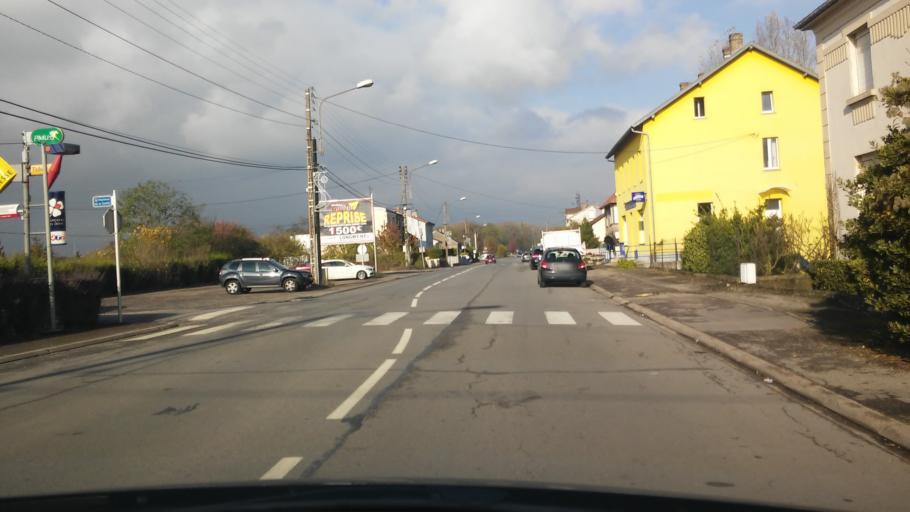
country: FR
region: Lorraine
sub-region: Departement de la Moselle
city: Richemont
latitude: 49.2807
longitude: 6.1689
